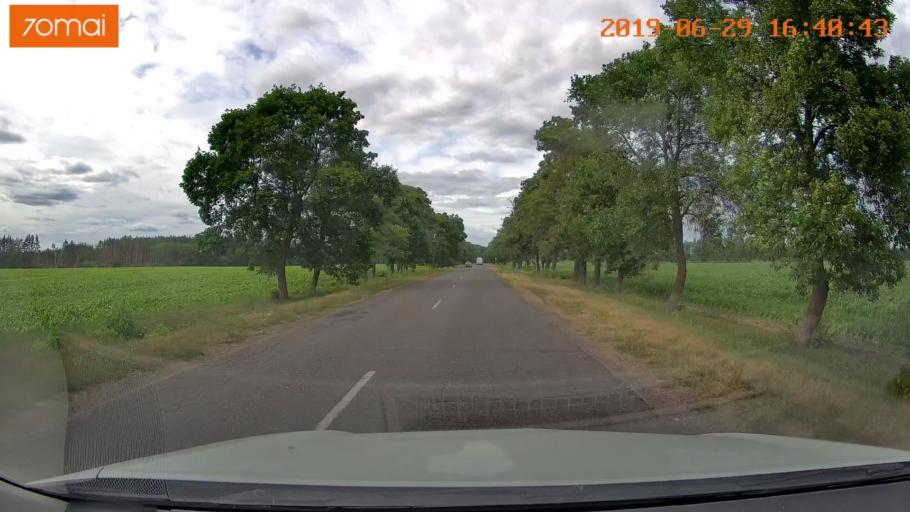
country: BY
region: Brest
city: Luninyets
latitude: 52.2598
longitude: 27.0174
